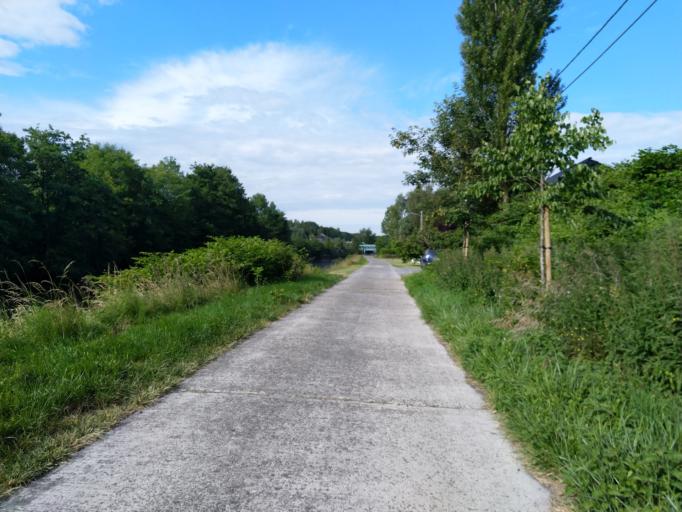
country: BE
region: Wallonia
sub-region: Province du Hainaut
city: Erquelinnes
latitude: 50.3034
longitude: 4.1155
